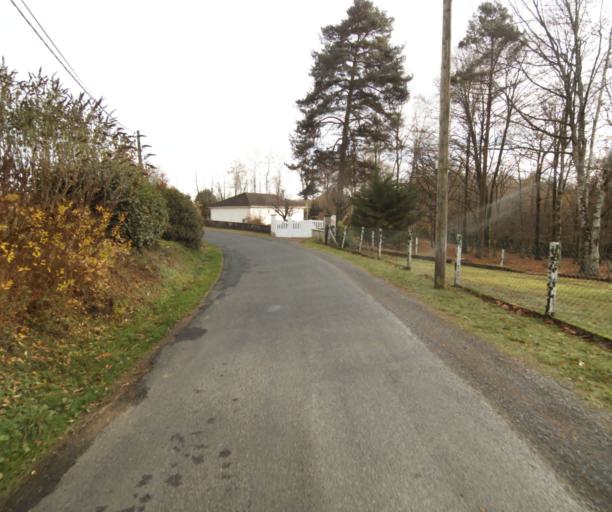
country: FR
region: Limousin
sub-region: Departement de la Correze
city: Sainte-Fortunade
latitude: 45.1915
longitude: 1.7857
